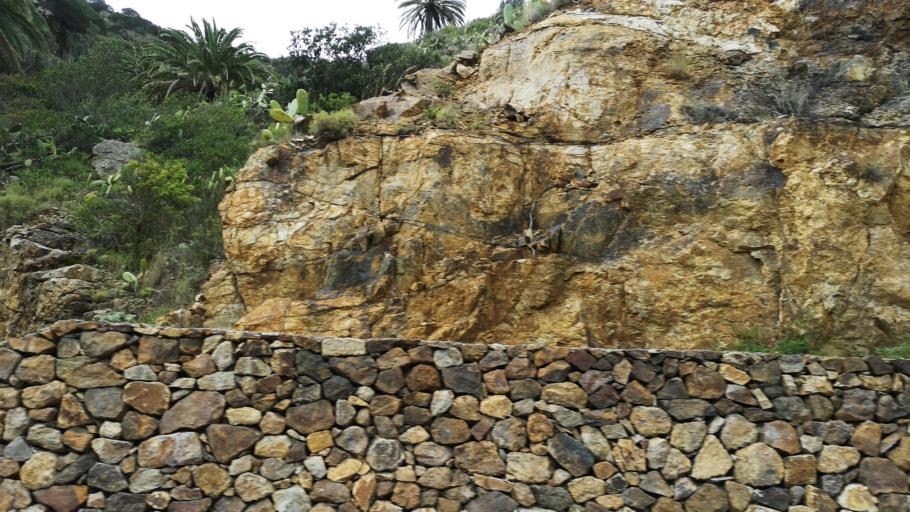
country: ES
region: Canary Islands
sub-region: Provincia de Santa Cruz de Tenerife
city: Vallehermosa
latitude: 28.1762
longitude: -17.2704
